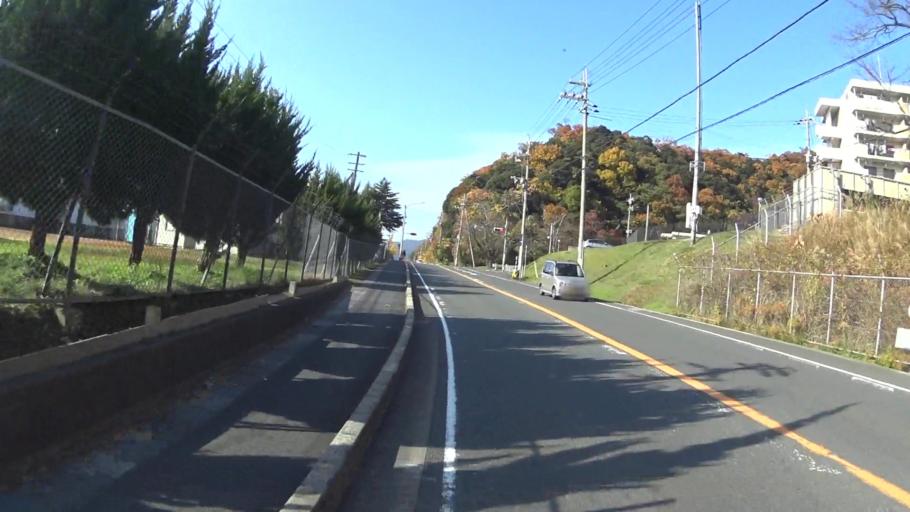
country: JP
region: Kyoto
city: Maizuru
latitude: 35.4850
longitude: 135.4010
